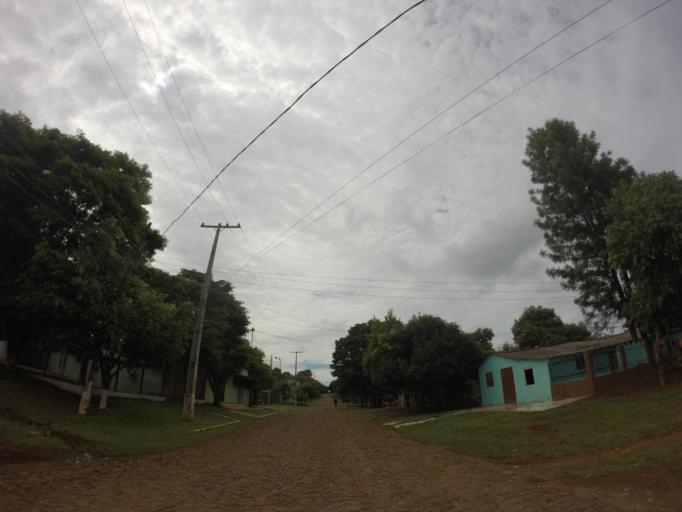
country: PY
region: Alto Parana
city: Ciudad del Este
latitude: -25.4041
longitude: -54.6516
